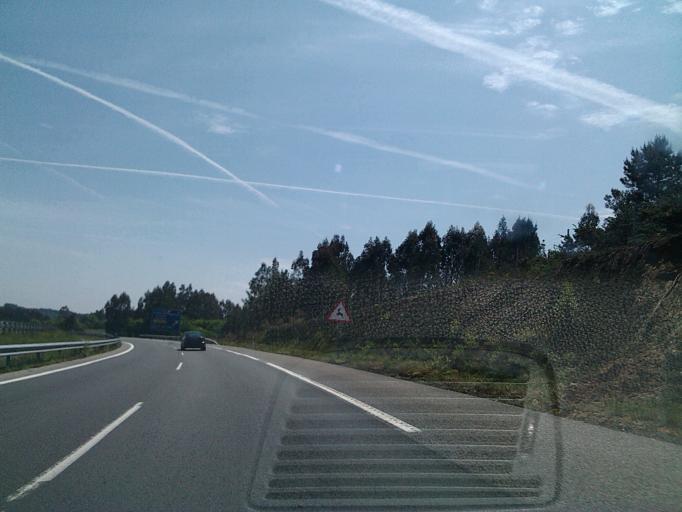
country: ES
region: Galicia
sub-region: Provincia da Coruna
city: Oroso
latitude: 42.9103
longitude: -8.4516
